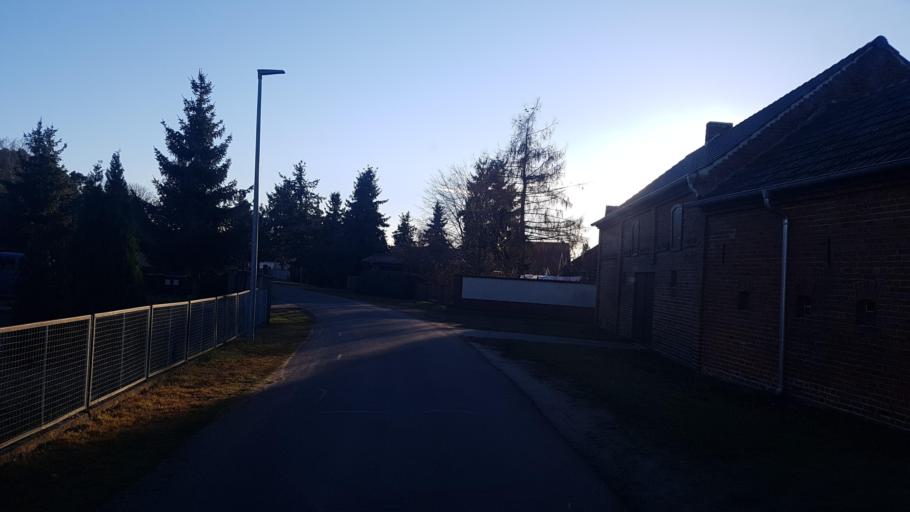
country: DE
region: Brandenburg
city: Peitz
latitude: 51.8868
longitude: 14.4184
